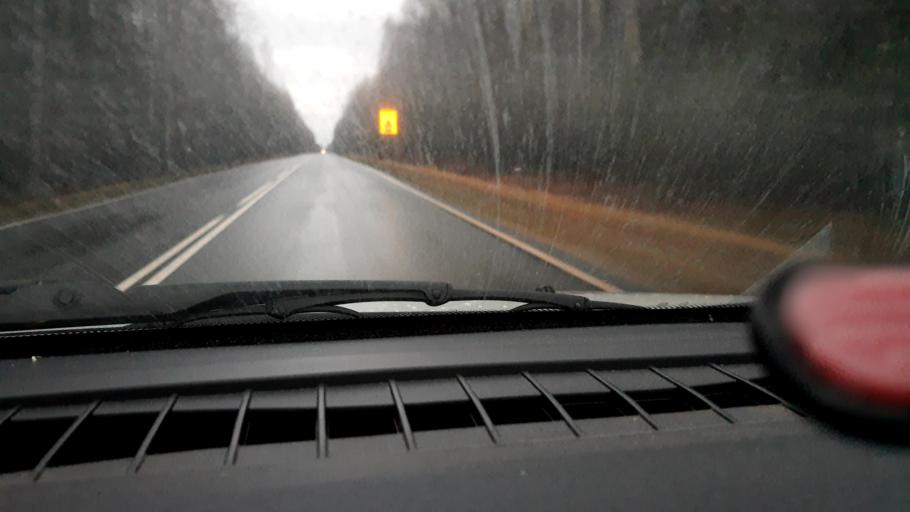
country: RU
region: Nizjnij Novgorod
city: Uren'
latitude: 57.2573
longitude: 45.6114
